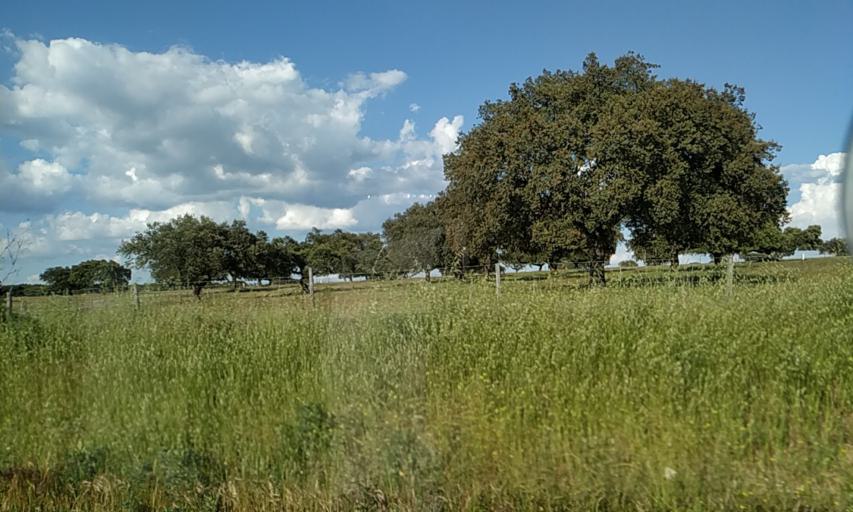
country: PT
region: Portalegre
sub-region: Portalegre
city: Urra
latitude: 39.1452
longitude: -7.4522
